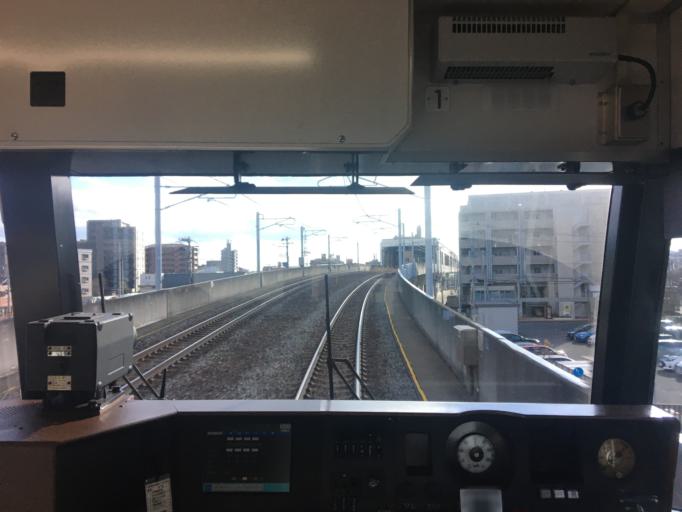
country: JP
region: Miyagi
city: Sendai
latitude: 38.2156
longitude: 140.8710
